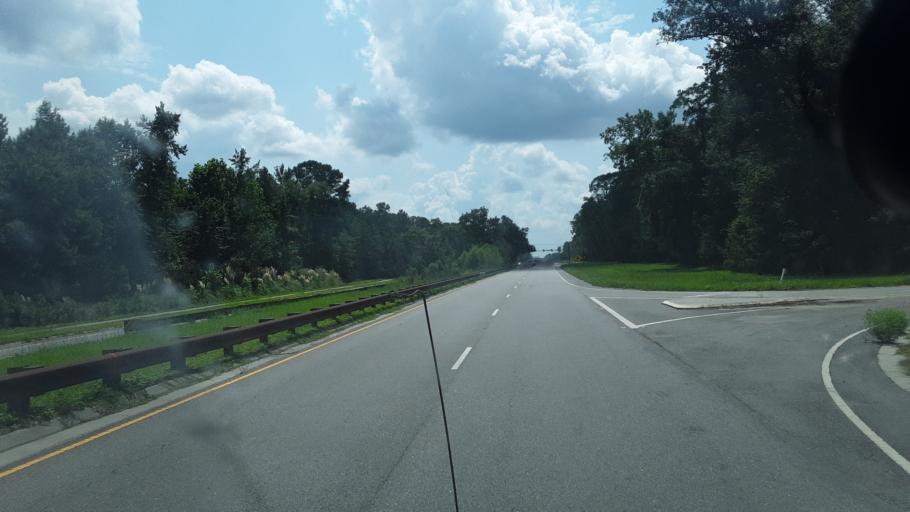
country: US
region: South Carolina
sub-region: Beaufort County
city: Bluffton
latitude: 32.2732
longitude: -80.9499
